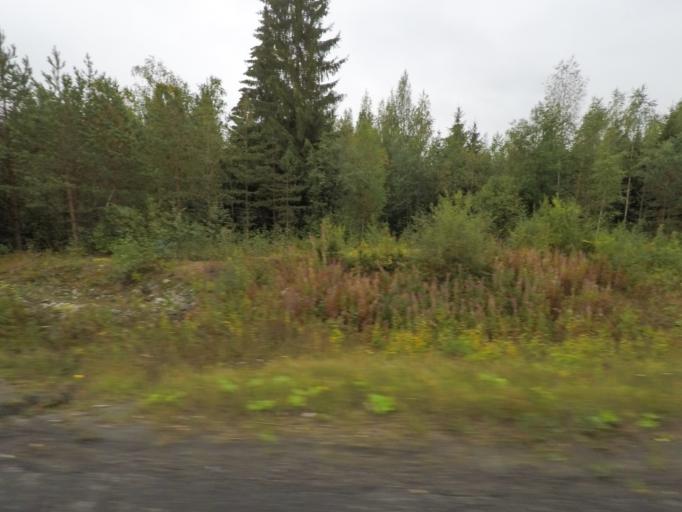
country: FI
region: Southern Savonia
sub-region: Mikkeli
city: Mikkeli
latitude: 61.7049
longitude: 27.3345
